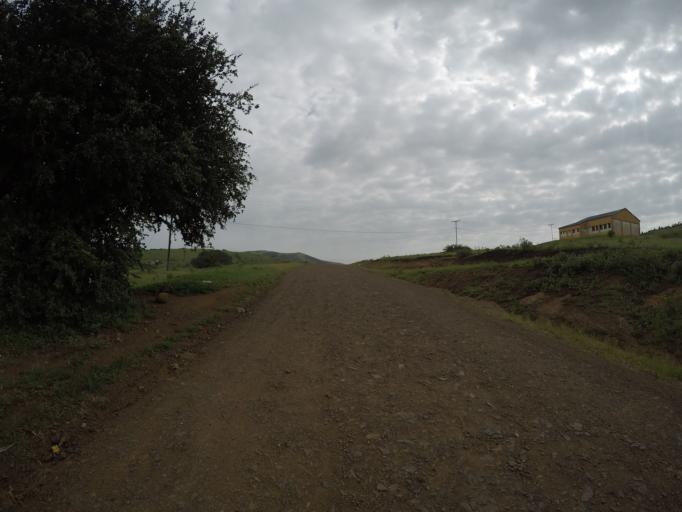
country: ZA
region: KwaZulu-Natal
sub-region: uThungulu District Municipality
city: Empangeni
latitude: -28.6325
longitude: 31.9049
